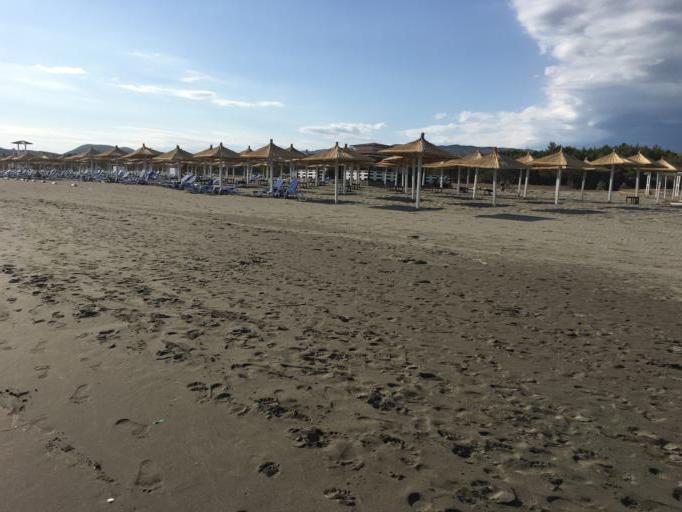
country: ME
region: Ulcinj
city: Ulcinj
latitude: 41.9034
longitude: 19.2630
